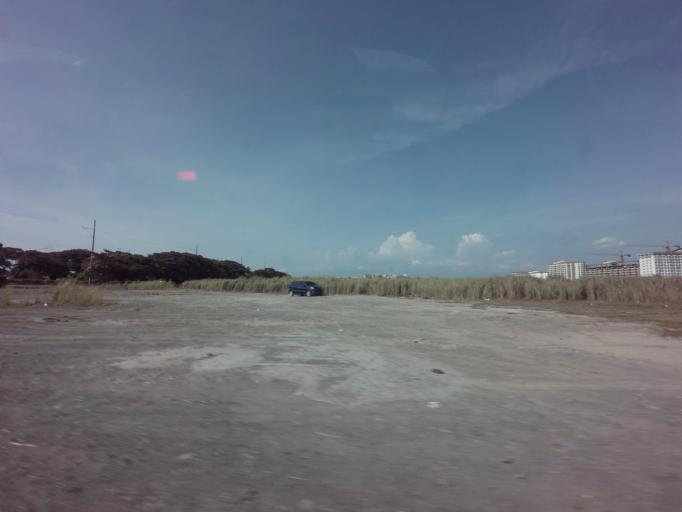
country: PH
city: Sambayanihan People's Village
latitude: 14.4785
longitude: 120.9862
